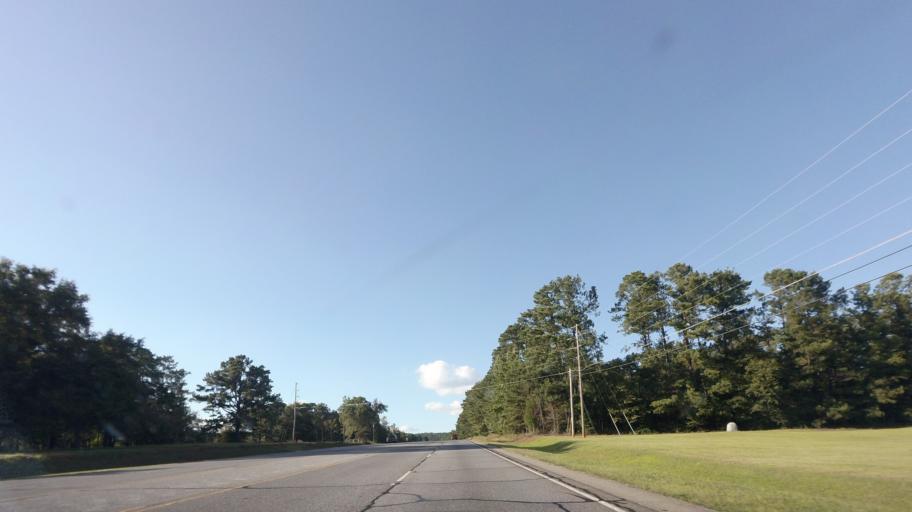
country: US
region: Georgia
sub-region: Upson County
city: Hannahs Mill
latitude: 32.9837
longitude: -84.3172
